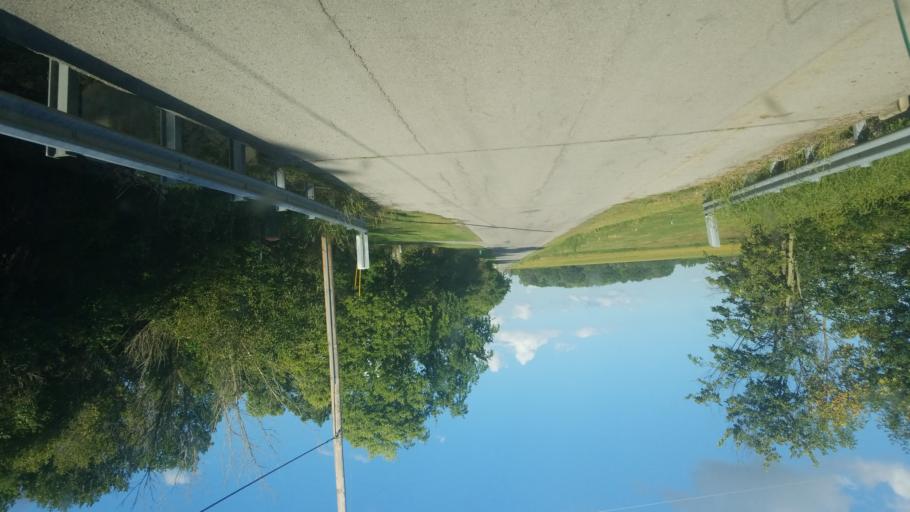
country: US
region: Ohio
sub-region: Hancock County
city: Arlington
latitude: 40.9359
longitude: -83.6702
